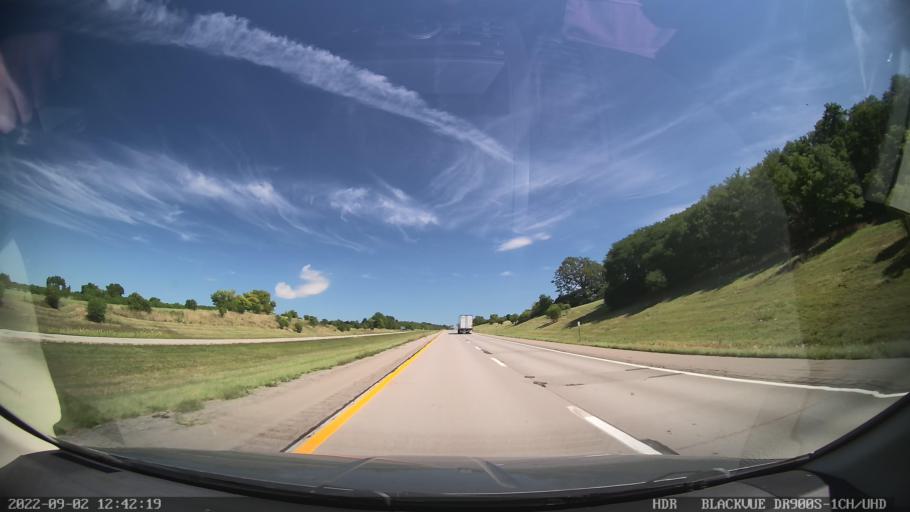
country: US
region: New York
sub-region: Livingston County
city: Geneseo
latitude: 42.7663
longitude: -77.8259
